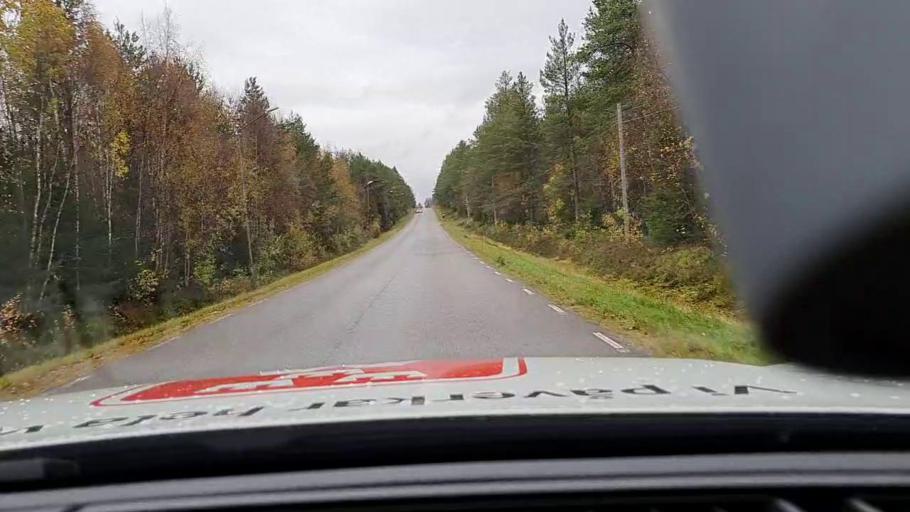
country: SE
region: Norrbotten
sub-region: Haparanda Kommun
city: Haparanda
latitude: 65.7864
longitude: 23.9210
